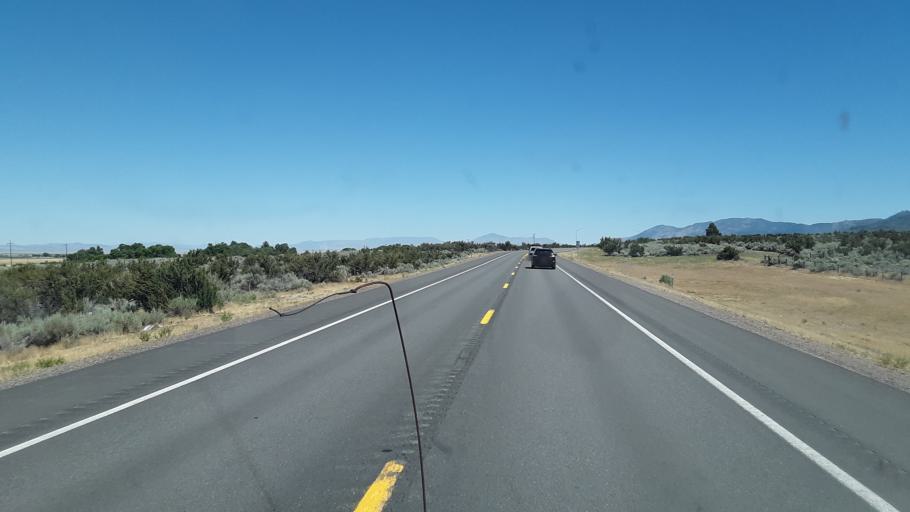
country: US
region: California
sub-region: Lassen County
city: Janesville
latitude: 40.2863
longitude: -120.4950
